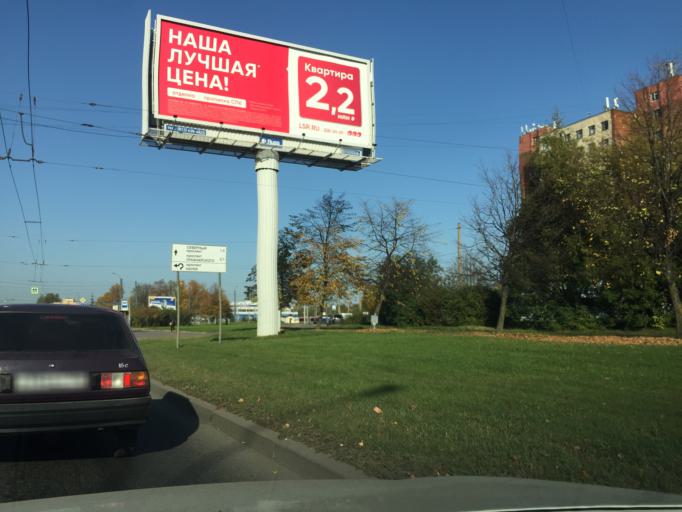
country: RU
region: Leningrad
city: Akademicheskoe
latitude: 60.0021
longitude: 30.4367
